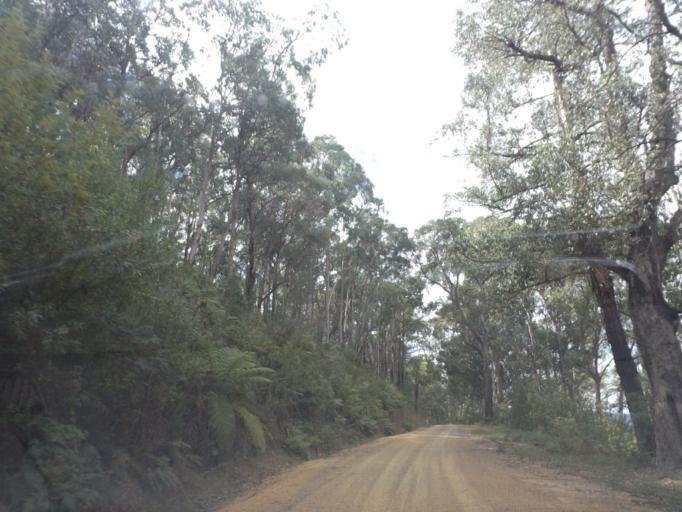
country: AU
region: Victoria
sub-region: Murrindindi
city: Alexandra
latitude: -37.4196
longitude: 145.9708
